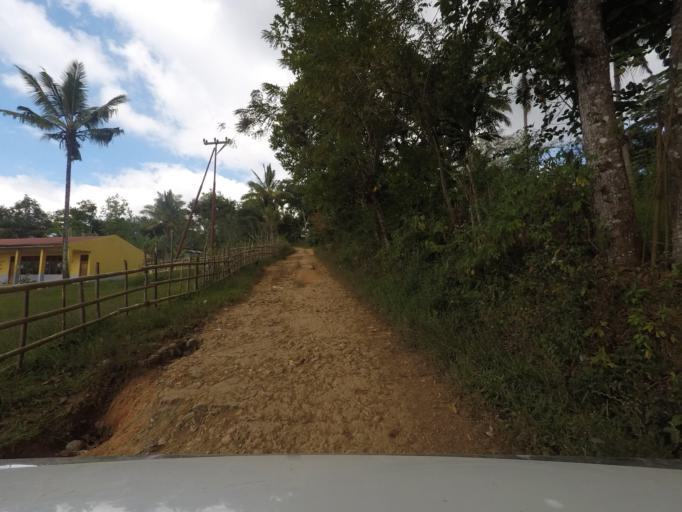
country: TL
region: Ermera
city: Gleno
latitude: -8.7213
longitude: 125.3231
